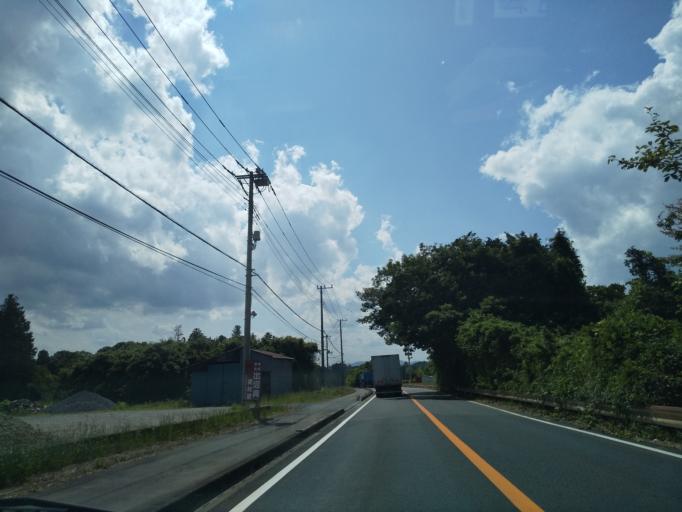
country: JP
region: Ibaraki
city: Ishioka
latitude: 36.1616
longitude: 140.3765
